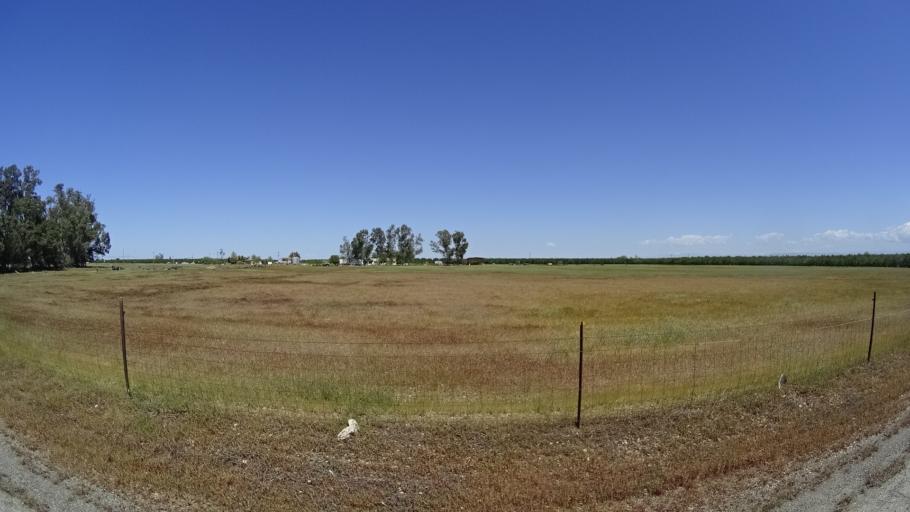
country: US
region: California
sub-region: Glenn County
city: Orland
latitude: 39.7214
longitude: -122.1383
